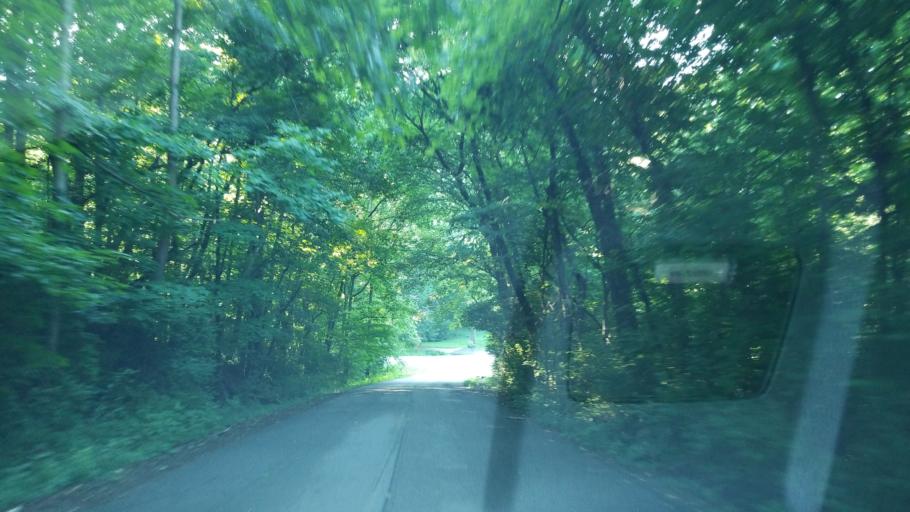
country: US
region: Tennessee
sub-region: Williamson County
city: Brentwood
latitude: 36.0423
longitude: -86.7913
